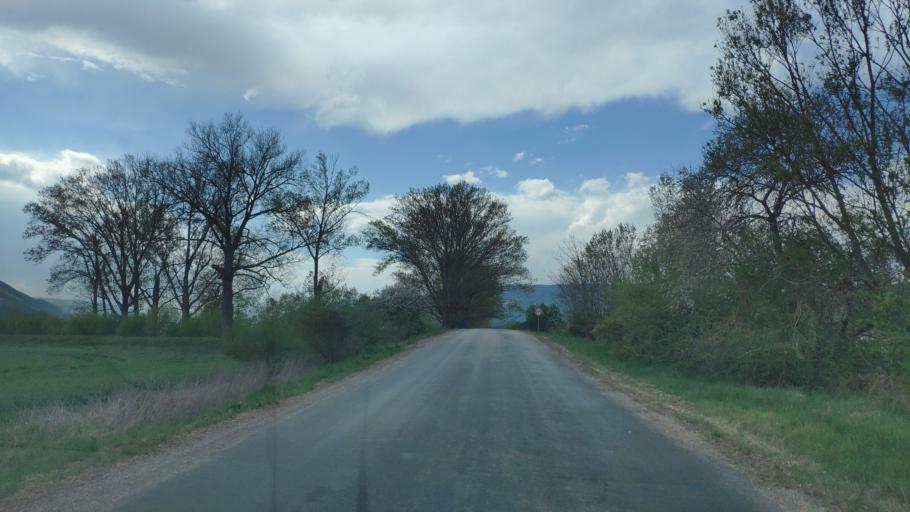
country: SK
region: Kosicky
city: Moldava nad Bodvou
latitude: 48.5934
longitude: 20.8949
